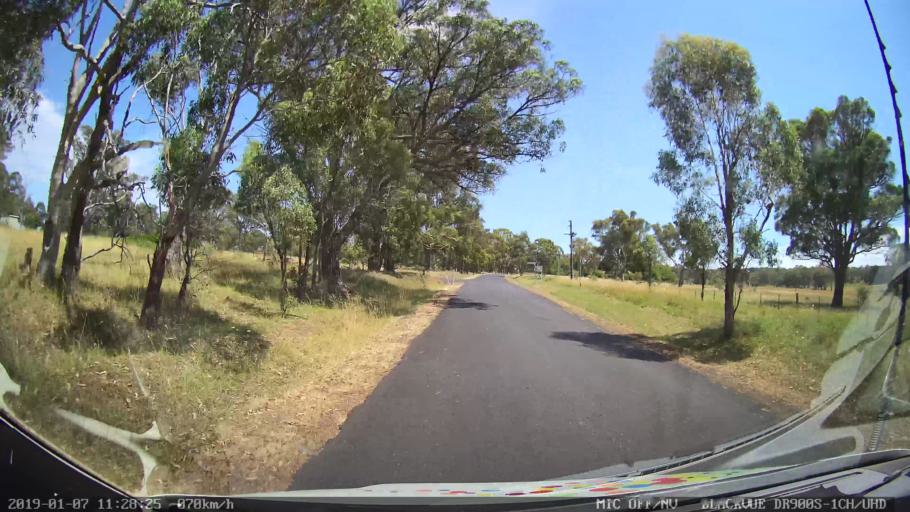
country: AU
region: New South Wales
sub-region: Armidale Dumaresq
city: Armidale
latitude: -30.4488
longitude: 151.5664
